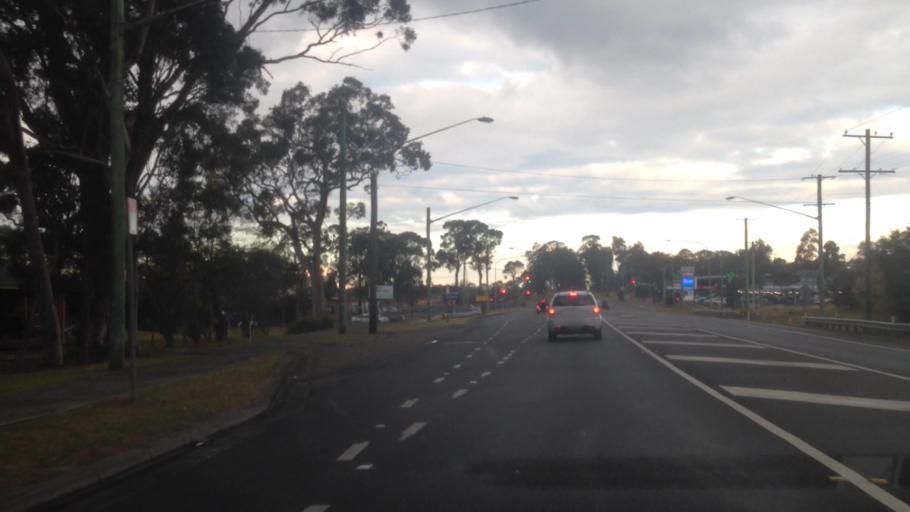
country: AU
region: New South Wales
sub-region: Wyong Shire
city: Tuggerawong
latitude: -33.2625
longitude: 151.4625
